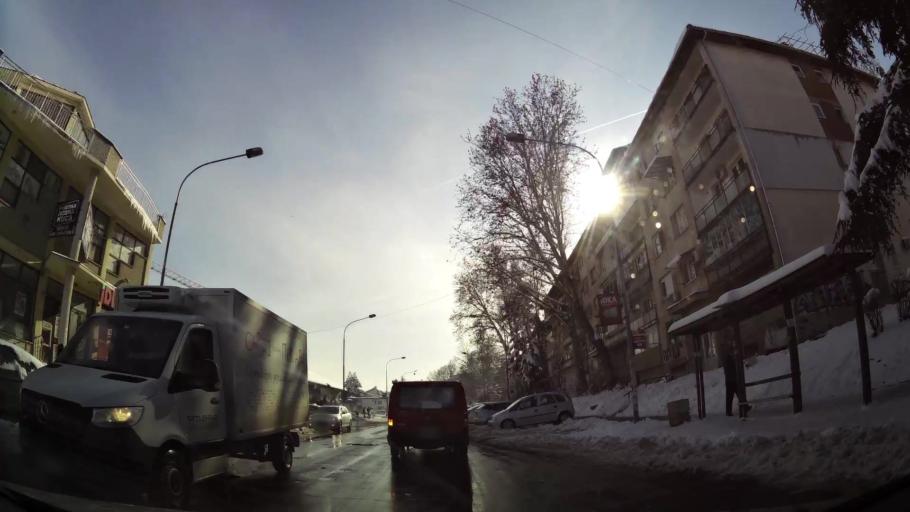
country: RS
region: Central Serbia
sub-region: Belgrade
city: Palilula
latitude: 44.8050
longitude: 20.5249
